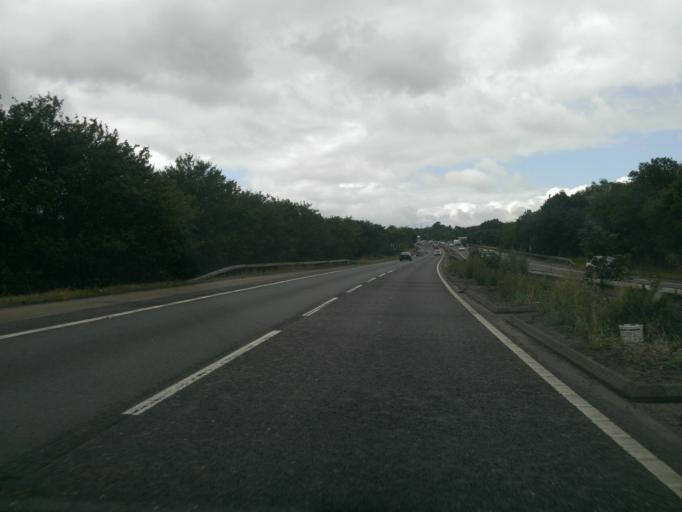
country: GB
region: England
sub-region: Essex
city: West Bergholt
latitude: 51.8975
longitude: 0.8599
